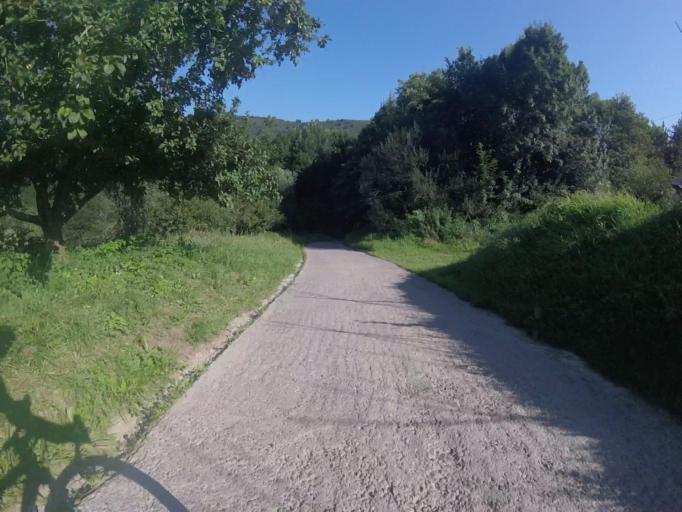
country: ES
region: Basque Country
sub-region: Provincia de Guipuzcoa
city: Astigarraga
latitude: 43.2558
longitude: -1.9395
